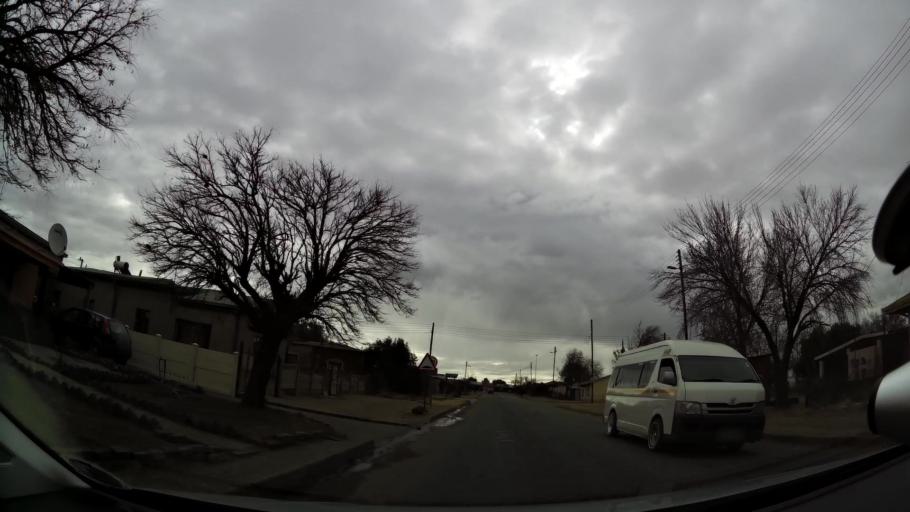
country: ZA
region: Orange Free State
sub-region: Fezile Dabi District Municipality
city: Kroonstad
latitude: -27.6529
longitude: 27.2089
